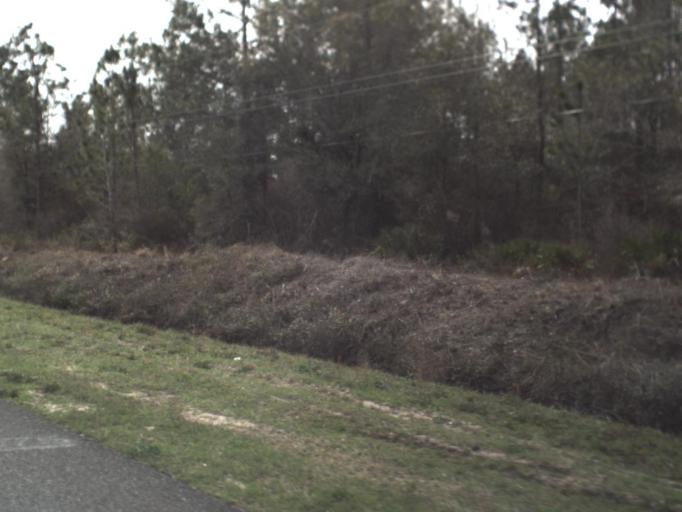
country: US
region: Florida
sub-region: Bay County
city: Youngstown
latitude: 30.5047
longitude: -85.4131
